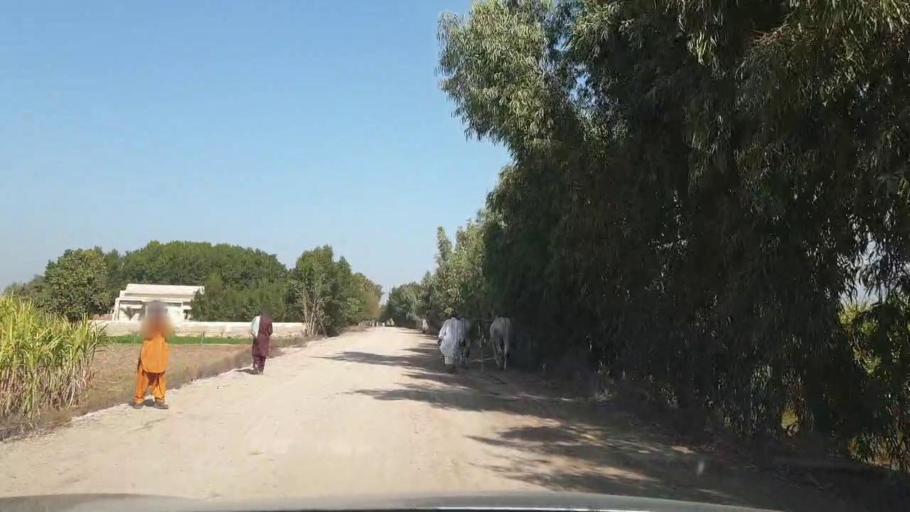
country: PK
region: Sindh
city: Tando Adam
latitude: 25.6100
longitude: 68.6437
